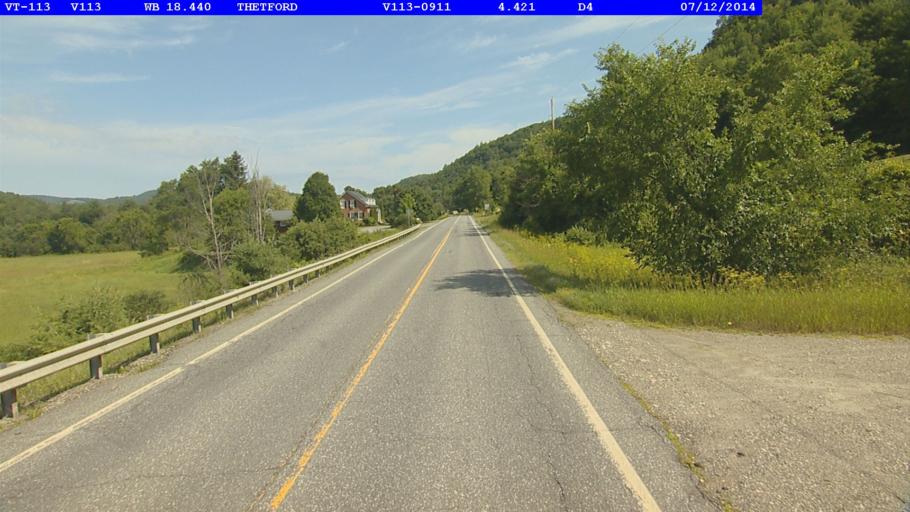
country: US
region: New Hampshire
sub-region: Grafton County
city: Lyme
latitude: 43.8380
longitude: -72.2470
